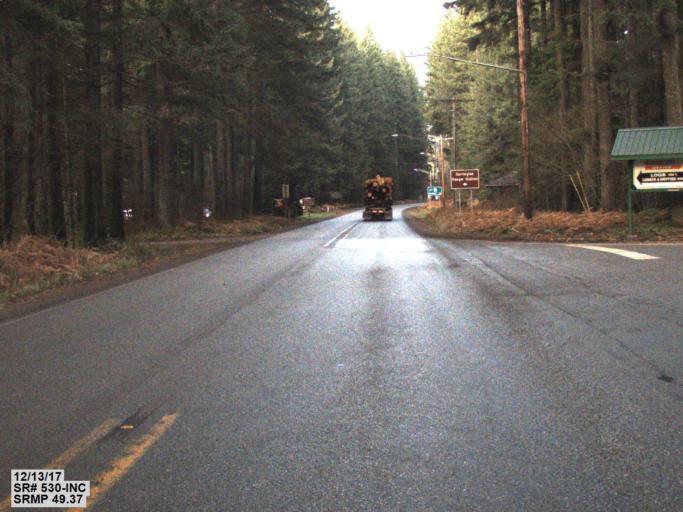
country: US
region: Washington
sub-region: Snohomish County
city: Darrington
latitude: 48.2596
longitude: -121.6020
